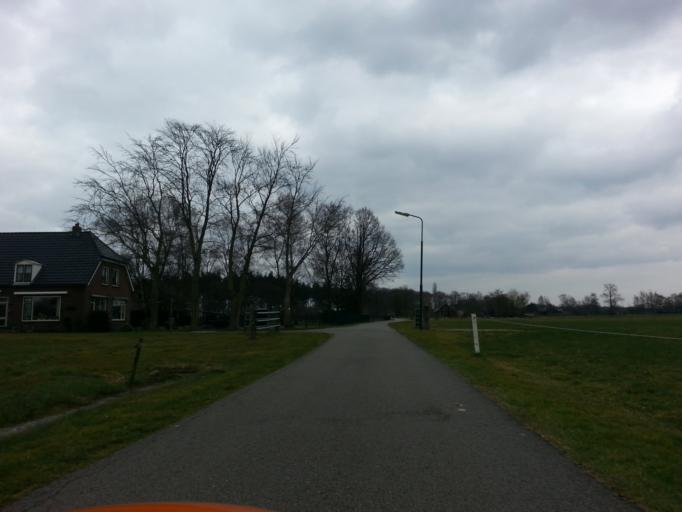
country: NL
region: Utrecht
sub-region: Gemeente Leusden
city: Leusden
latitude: 52.1141
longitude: 5.4873
